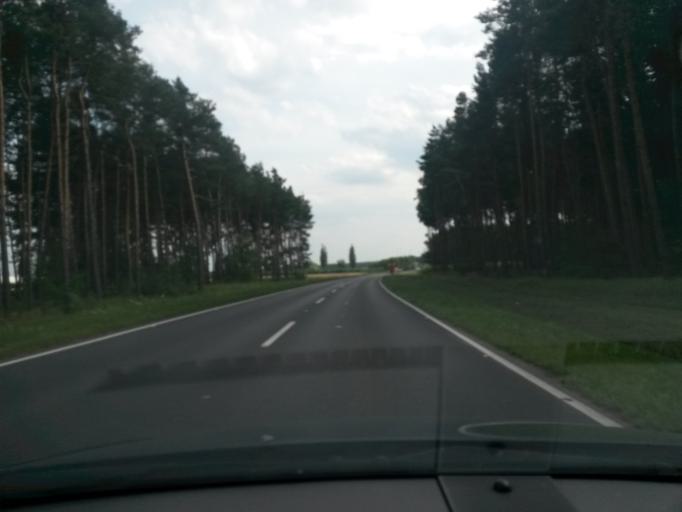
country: PL
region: Greater Poland Voivodeship
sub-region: Powiat poznanski
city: Kornik
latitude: 52.2221
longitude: 17.0735
